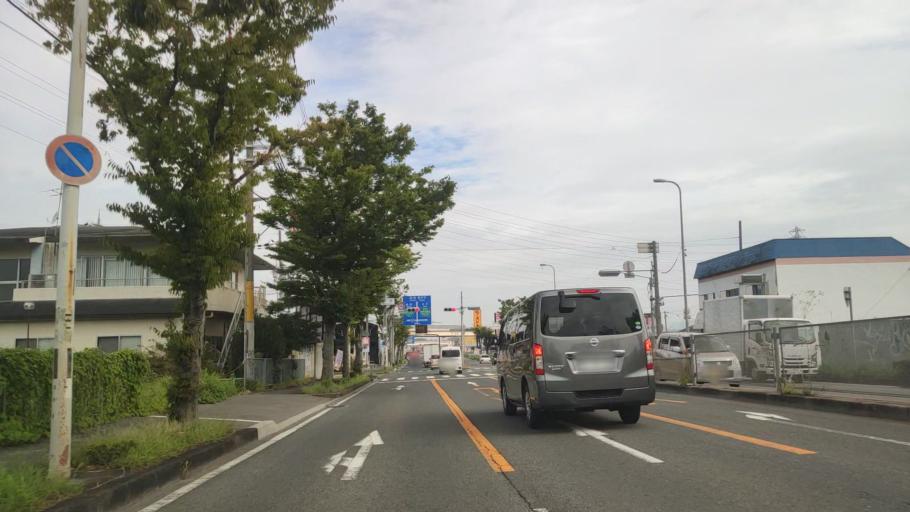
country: JP
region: Osaka
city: Tondabayashicho
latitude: 34.5300
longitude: 135.6049
